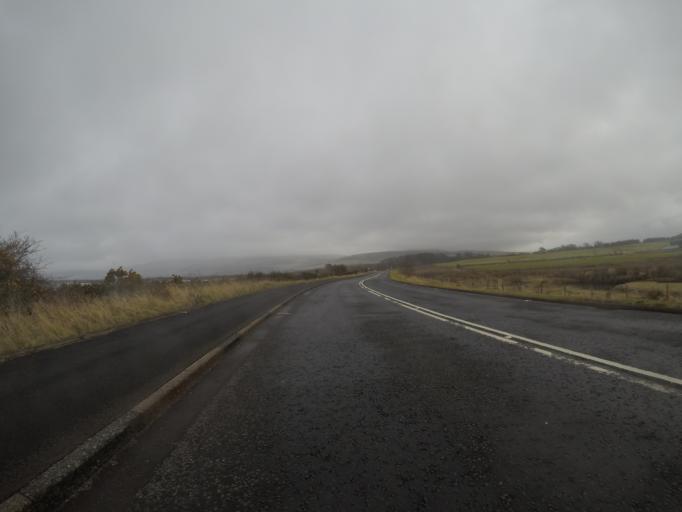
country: GB
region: Scotland
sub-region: North Ayrshire
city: Millport
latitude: 55.7272
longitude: -4.8934
